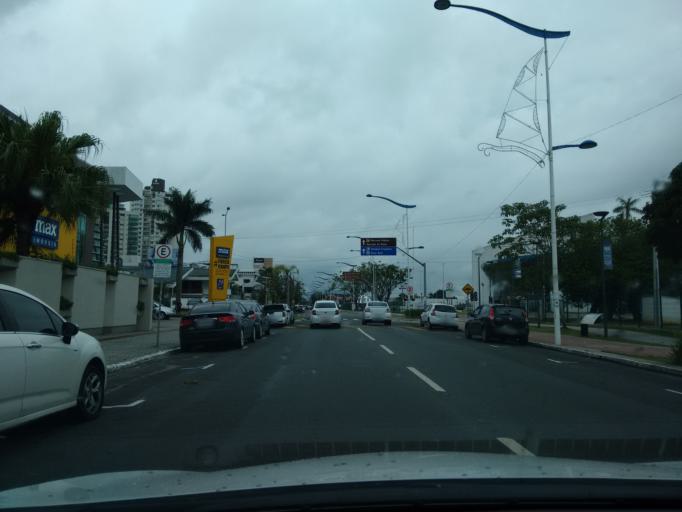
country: BR
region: Santa Catarina
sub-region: Itajai
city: Itajai
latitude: -26.9110
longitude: -48.6538
